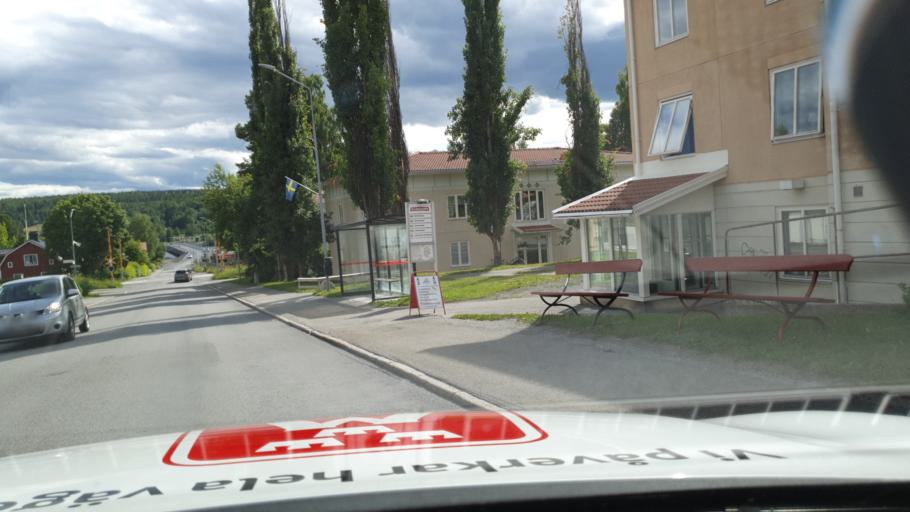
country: SE
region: Jaemtland
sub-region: OEstersunds Kommun
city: Lit
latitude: 63.3161
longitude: 14.8453
